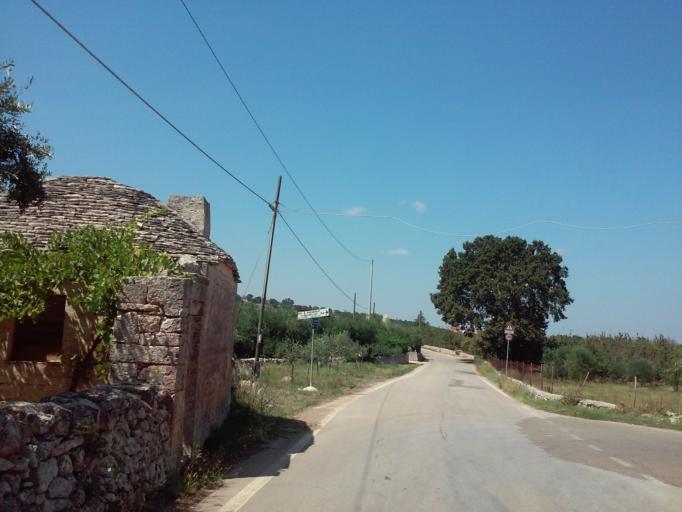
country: IT
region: Apulia
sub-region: Provincia di Bari
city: Alberobello
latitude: 40.7964
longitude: 17.2196
